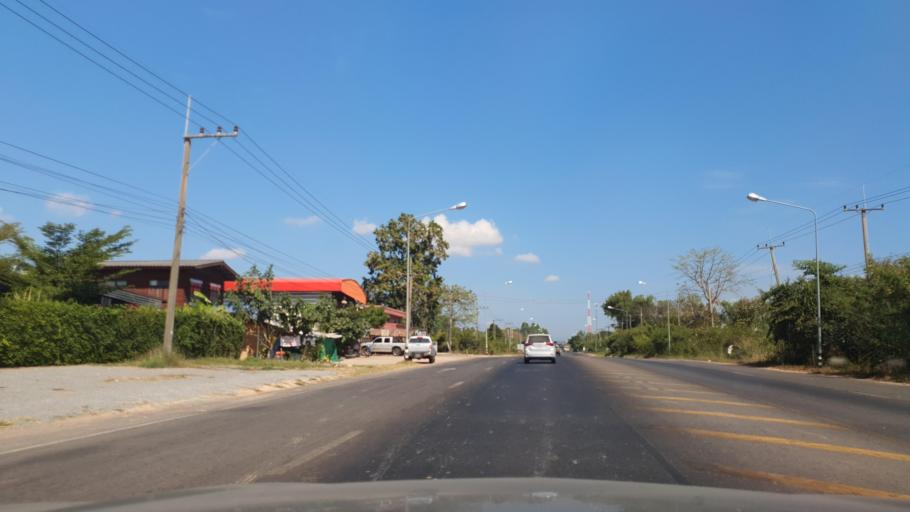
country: TH
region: Kalasin
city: Somdet
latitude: 16.7177
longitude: 103.7563
